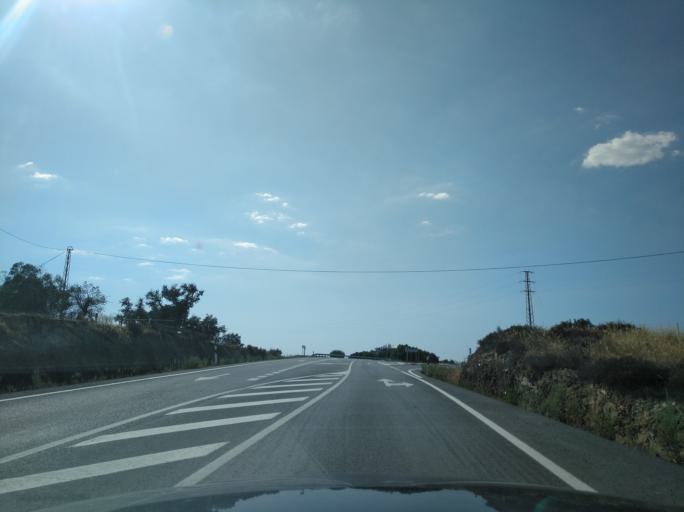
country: ES
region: Andalusia
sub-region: Provincia de Huelva
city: Santa Barbara de Casa
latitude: 37.7940
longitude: -7.1925
